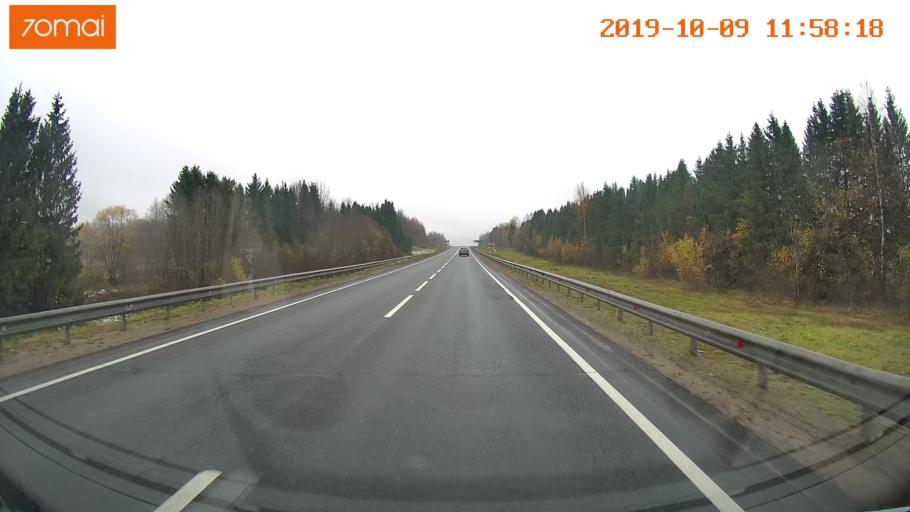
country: RU
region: Vologda
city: Gryazovets
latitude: 58.7200
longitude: 40.2963
